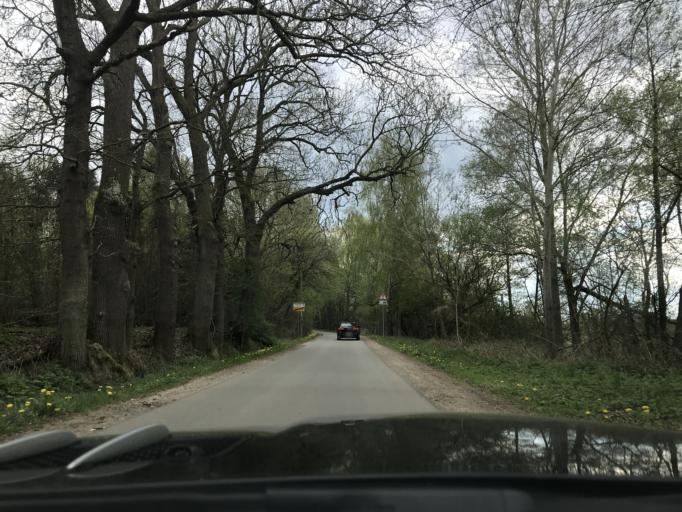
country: DE
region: Schleswig-Holstein
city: Gross Gronau
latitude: 53.7989
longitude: 10.7878
